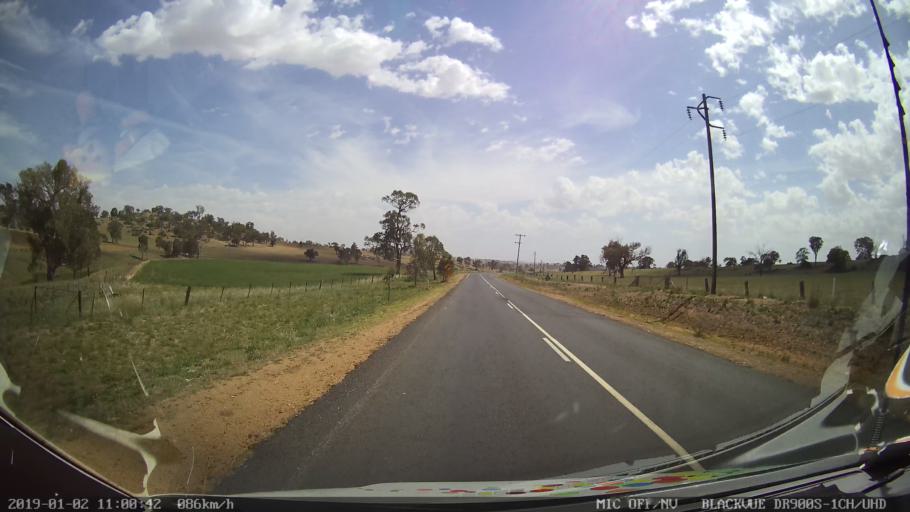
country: AU
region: New South Wales
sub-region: Cootamundra
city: Cootamundra
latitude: -34.6055
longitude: 148.3128
